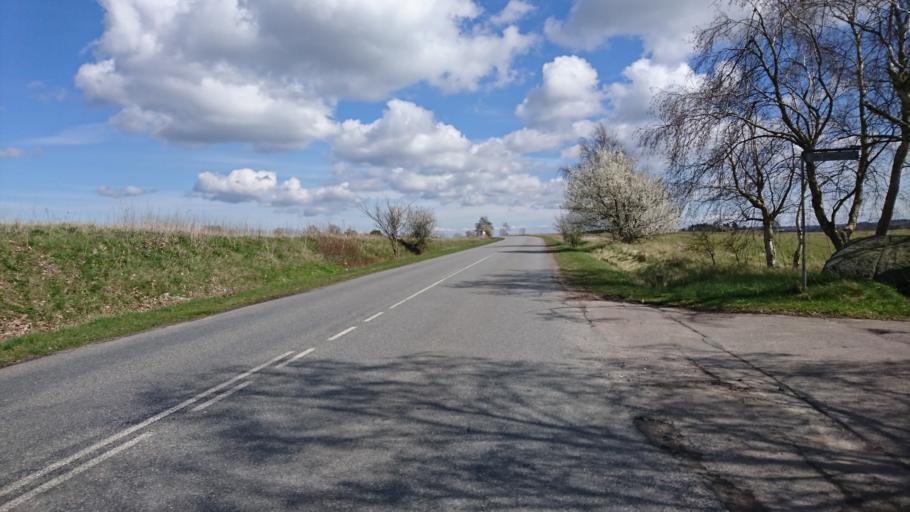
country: DK
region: Capital Region
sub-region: Egedal Kommune
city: Ganlose
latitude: 55.7823
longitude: 12.2737
